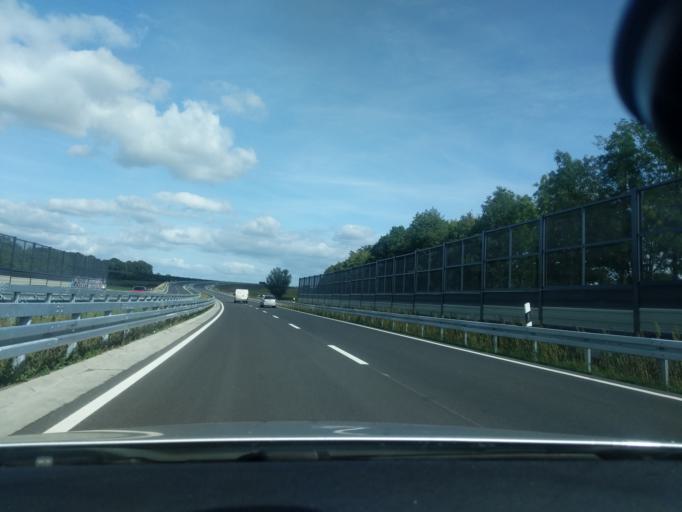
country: DE
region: Lower Saxony
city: Belm
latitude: 52.3169
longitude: 8.1374
